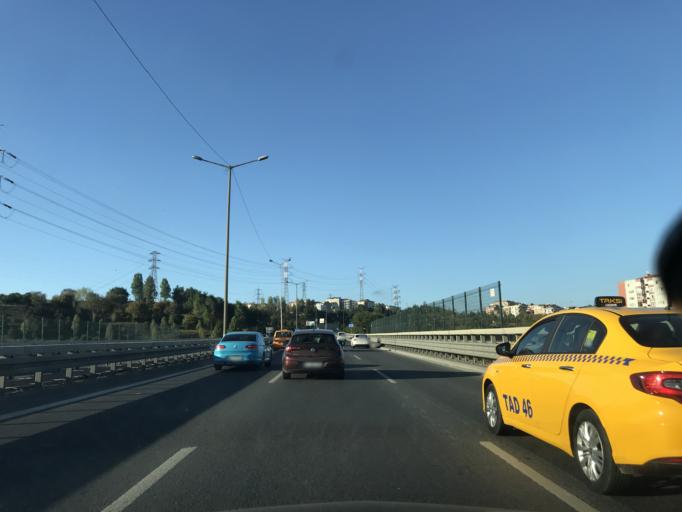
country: TR
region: Istanbul
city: Sisli
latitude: 41.0685
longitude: 28.9573
